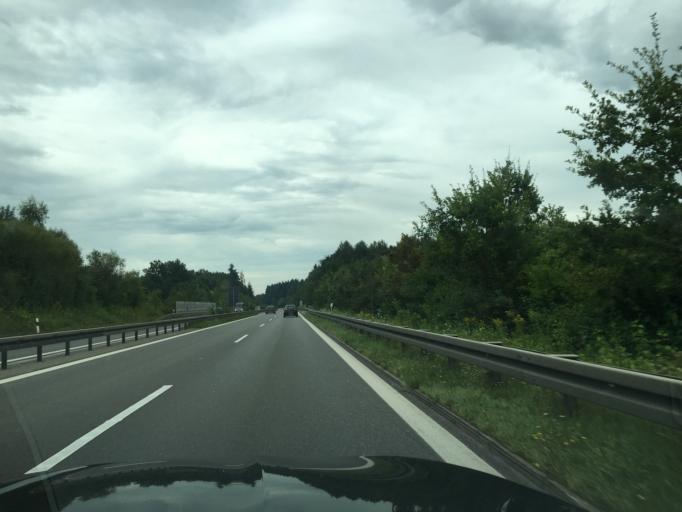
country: DE
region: Baden-Wuerttemberg
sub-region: Freiburg Region
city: Radolfzell am Bodensee
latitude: 47.7587
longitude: 8.9914
